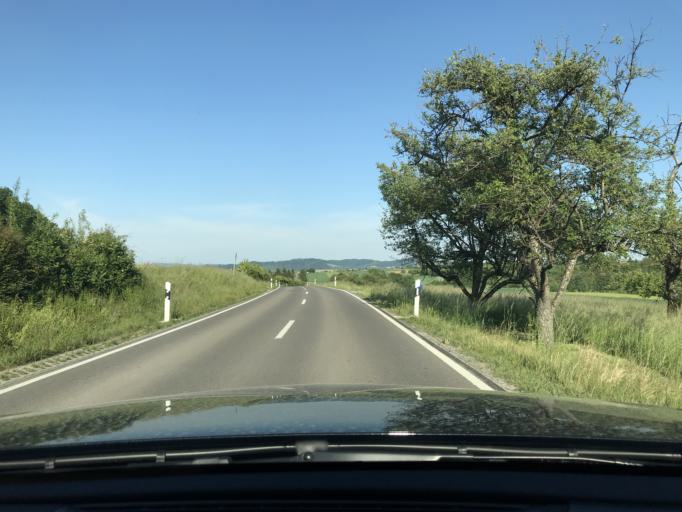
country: DE
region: Baden-Wuerttemberg
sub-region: Regierungsbezirk Stuttgart
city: Schwaikheim
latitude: 48.8920
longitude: 9.3456
